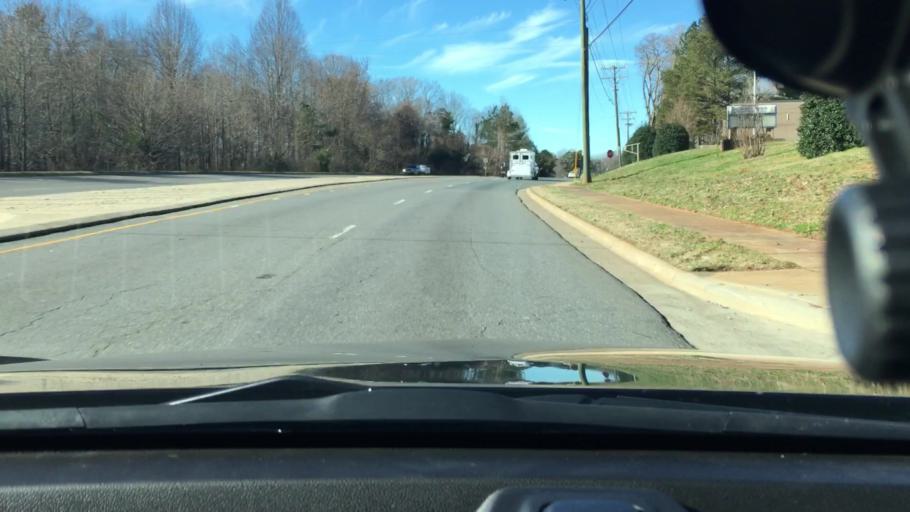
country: US
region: North Carolina
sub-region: Mecklenburg County
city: Mint Hill
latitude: 35.2233
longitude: -80.6244
